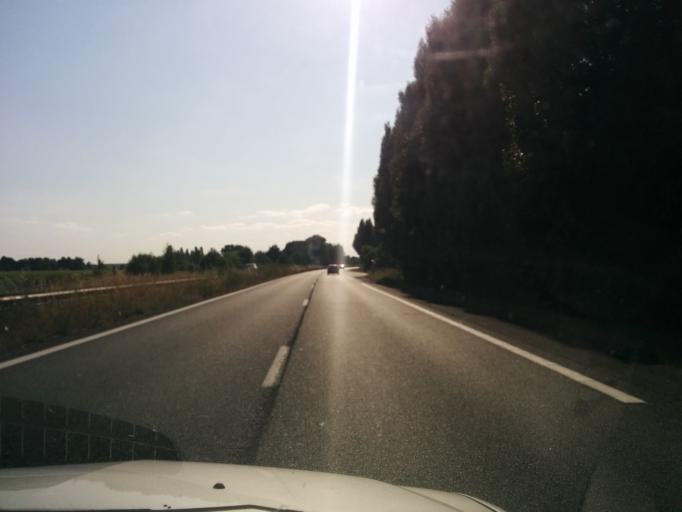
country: FR
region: Pays de la Loire
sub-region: Departement de la Loire-Atlantique
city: Mouzillon
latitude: 47.1563
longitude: -1.2873
